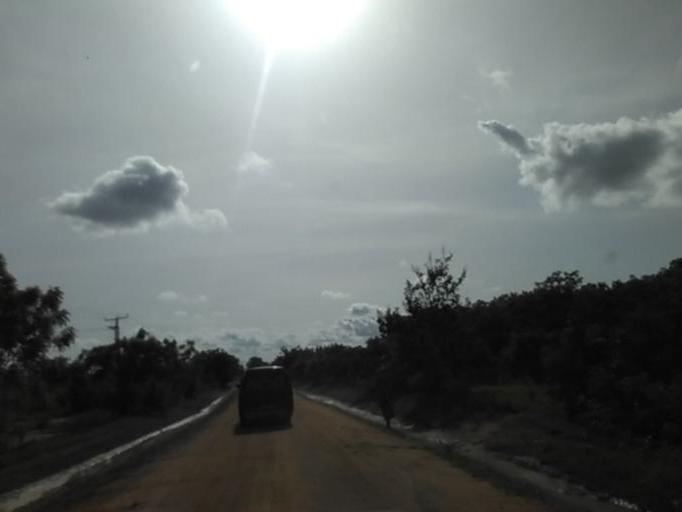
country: GH
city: Akropong
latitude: 6.0331
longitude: 0.3330
